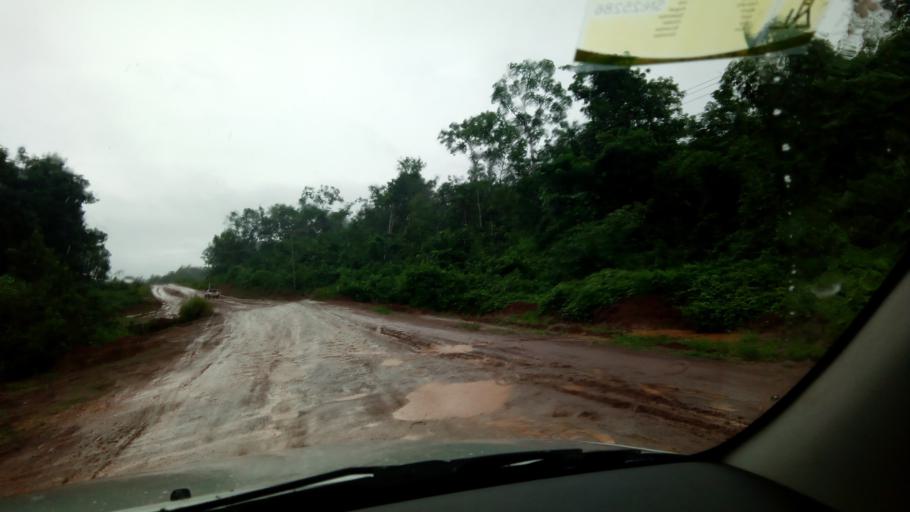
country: LR
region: Nimba
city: Sanniquellie
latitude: 7.0984
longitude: -8.8921
